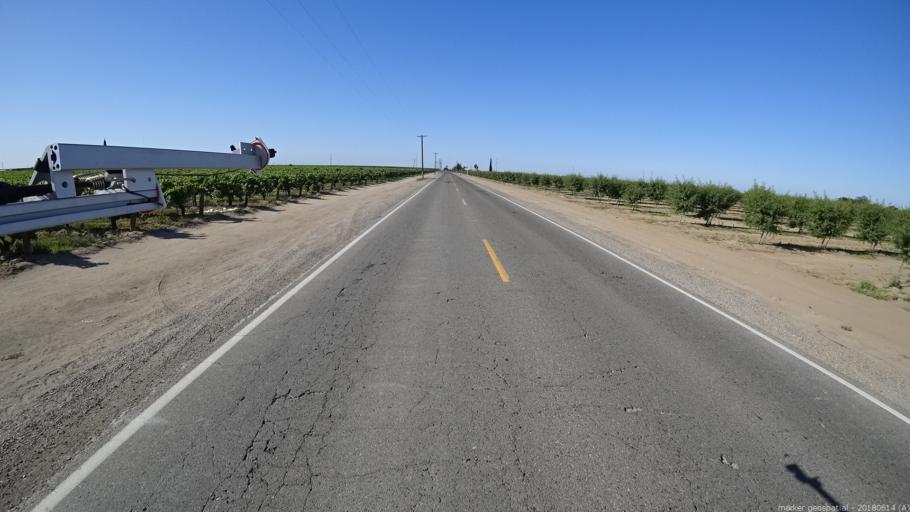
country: US
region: California
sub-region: Madera County
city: Madera
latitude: 36.9272
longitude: -120.1286
